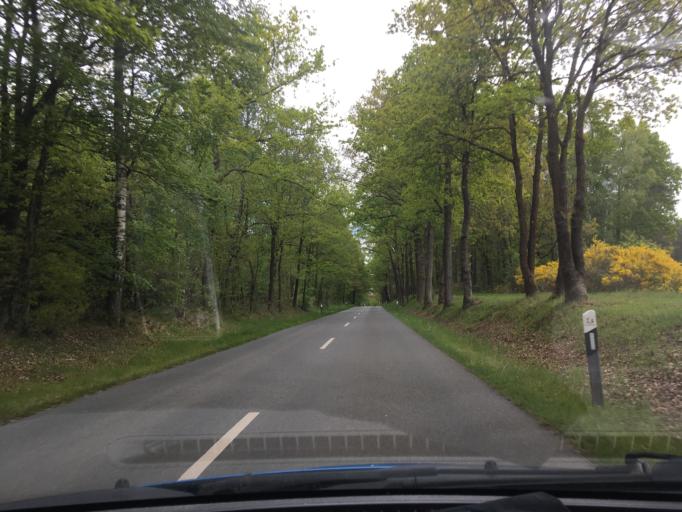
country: DE
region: Lower Saxony
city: Suderburg
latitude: 52.8731
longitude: 10.4346
